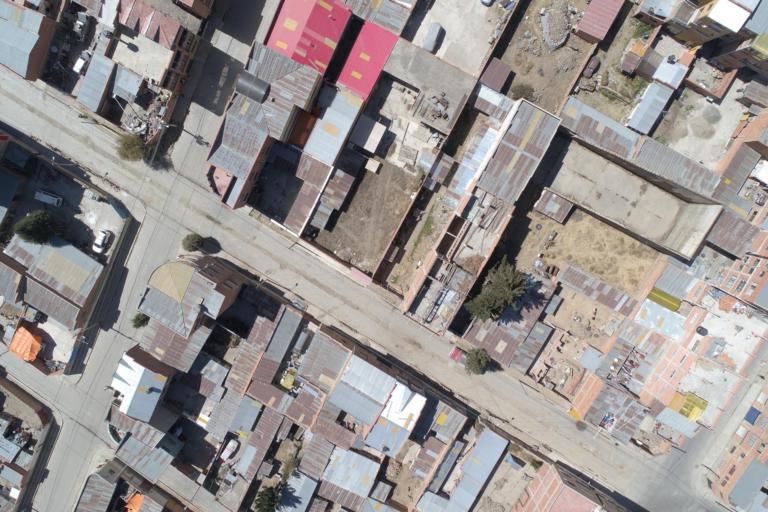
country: BO
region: La Paz
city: La Paz
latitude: -16.5280
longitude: -68.1612
